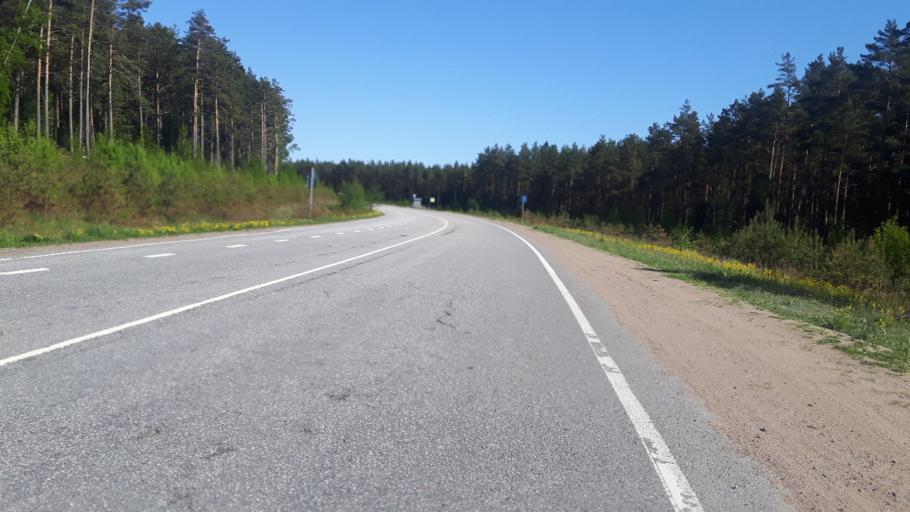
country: RU
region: Leningrad
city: Sosnovyy Bor
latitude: 60.1861
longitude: 29.0261
